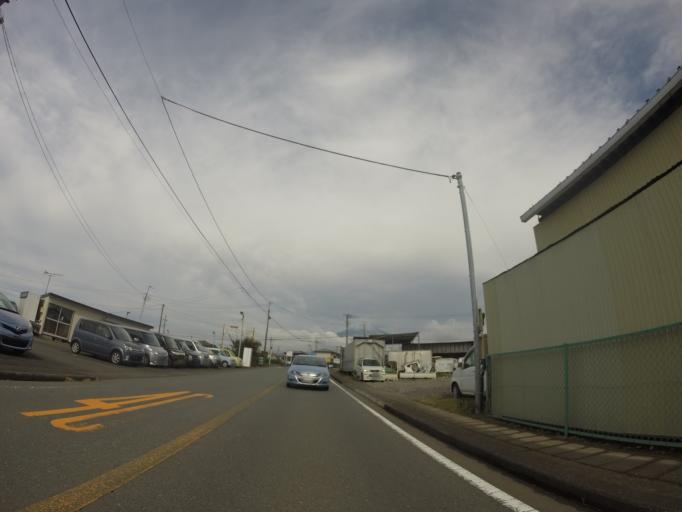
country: JP
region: Shizuoka
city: Fuji
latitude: 35.2062
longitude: 138.6844
